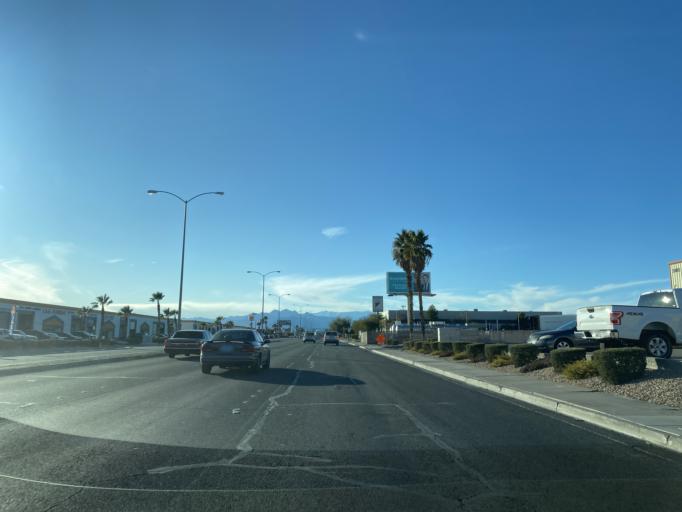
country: US
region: Nevada
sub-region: Clark County
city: Nellis Air Force Base
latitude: 36.2404
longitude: -115.0902
